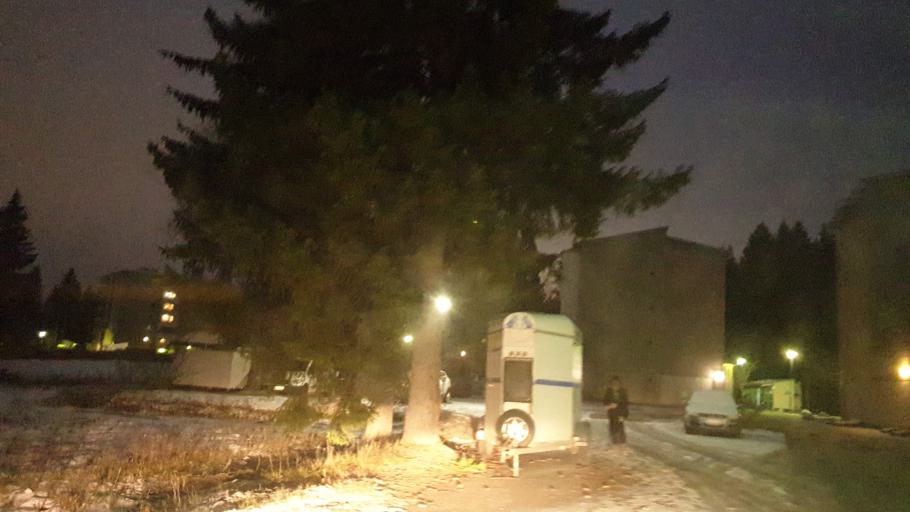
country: FI
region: Southern Savonia
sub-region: Savonlinna
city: Savonlinna
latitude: 61.8606
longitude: 28.9527
